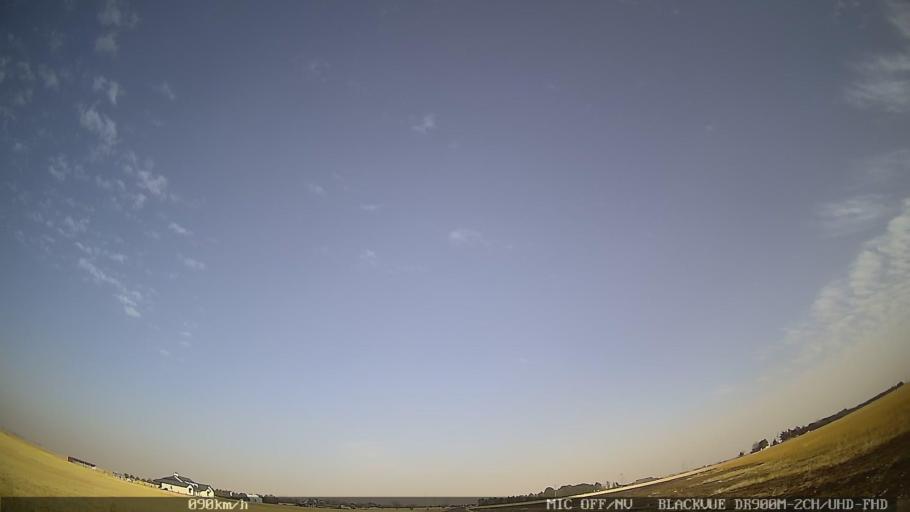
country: US
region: New Mexico
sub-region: Curry County
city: Texico
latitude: 34.4193
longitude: -103.1103
